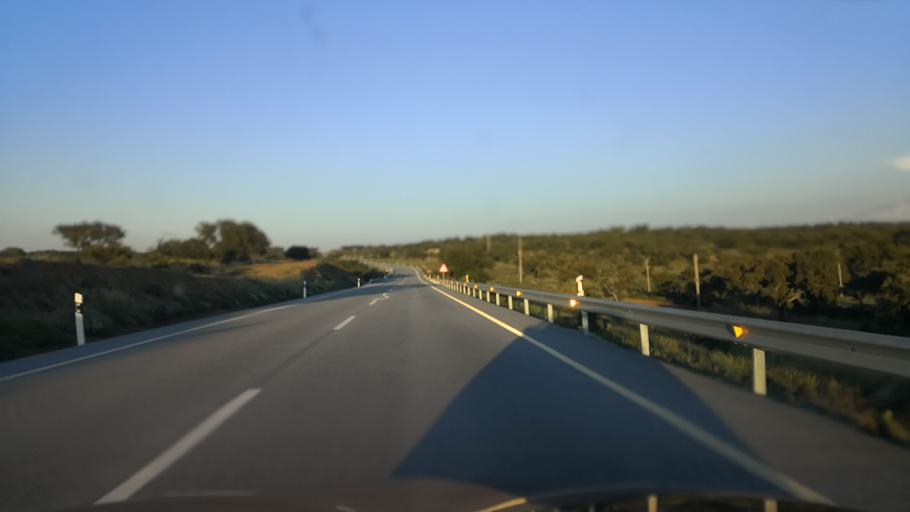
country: ES
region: Extremadura
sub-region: Provincia de Caceres
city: Salorino
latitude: 39.5133
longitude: -7.0863
